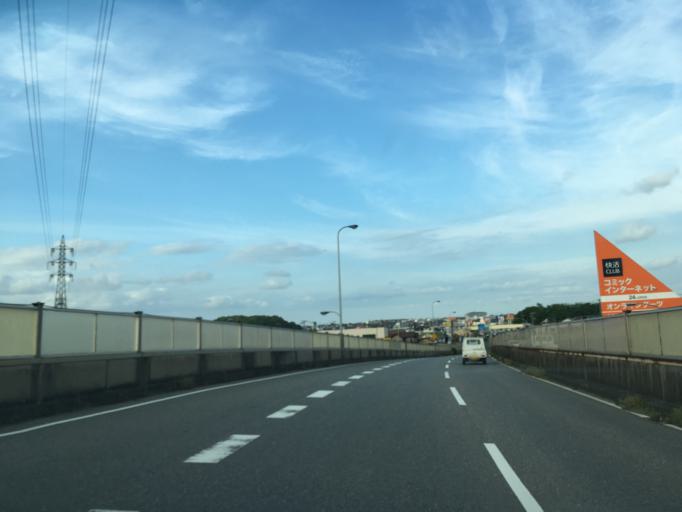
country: JP
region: Chiba
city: Kisarazu
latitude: 35.3726
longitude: 139.9331
